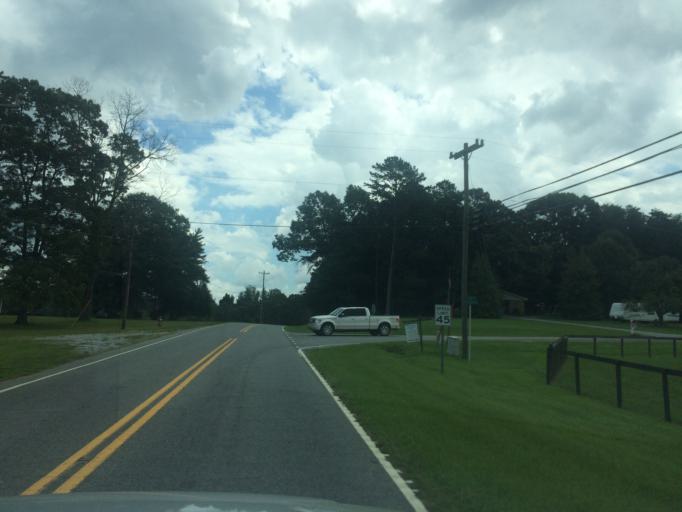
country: US
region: North Carolina
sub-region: Polk County
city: Columbus
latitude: 35.2283
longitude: -82.0630
